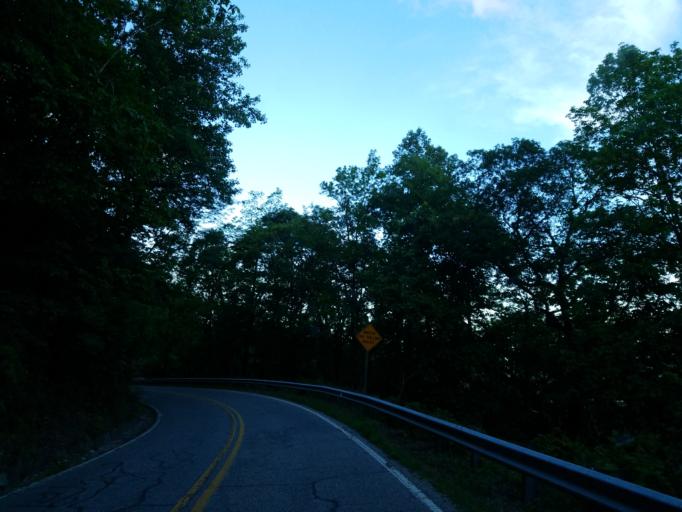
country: US
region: Georgia
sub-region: Lumpkin County
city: Dahlonega
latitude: 34.6769
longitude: -83.9988
